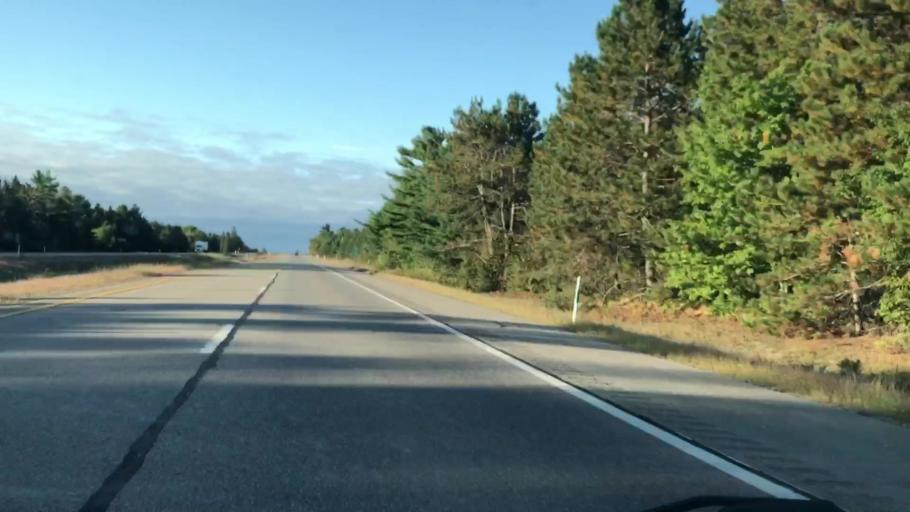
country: US
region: Michigan
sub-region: Chippewa County
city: Sault Ste. Marie
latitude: 46.4322
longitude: -84.3903
